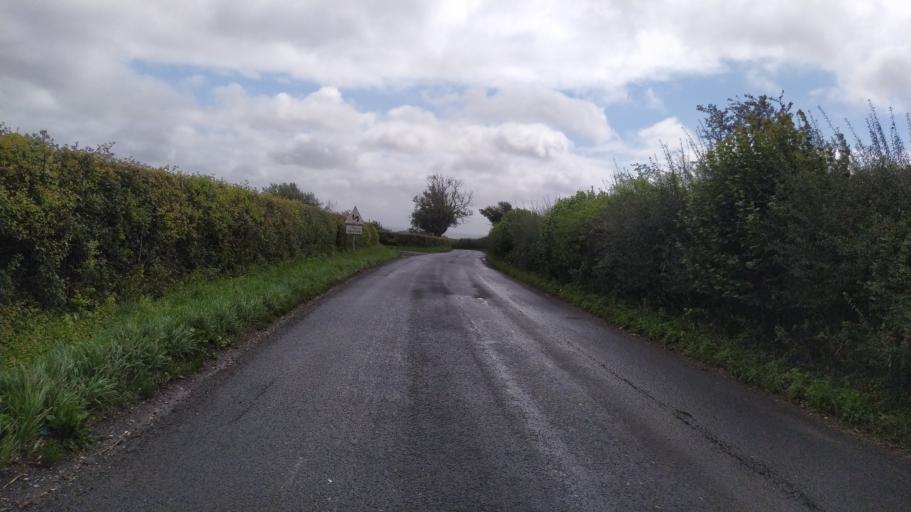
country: GB
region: England
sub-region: Wiltshire
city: Ansty
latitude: 50.9625
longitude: -2.1077
